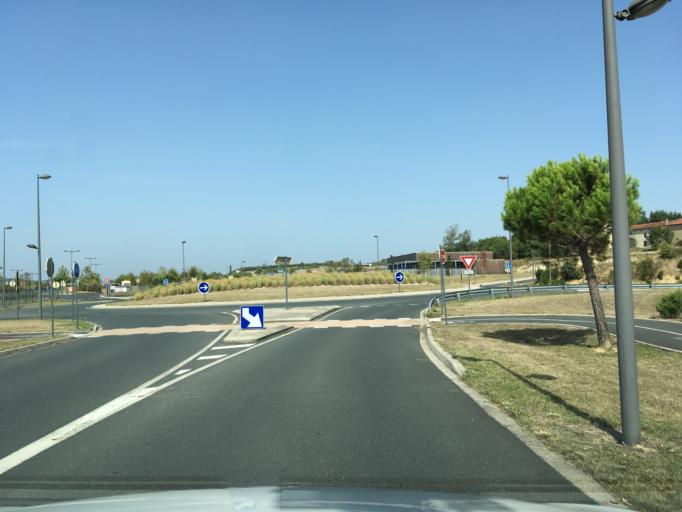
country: FR
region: Midi-Pyrenees
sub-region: Departement du Tarn
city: Lagarrigue
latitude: 43.5665
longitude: 2.2644
